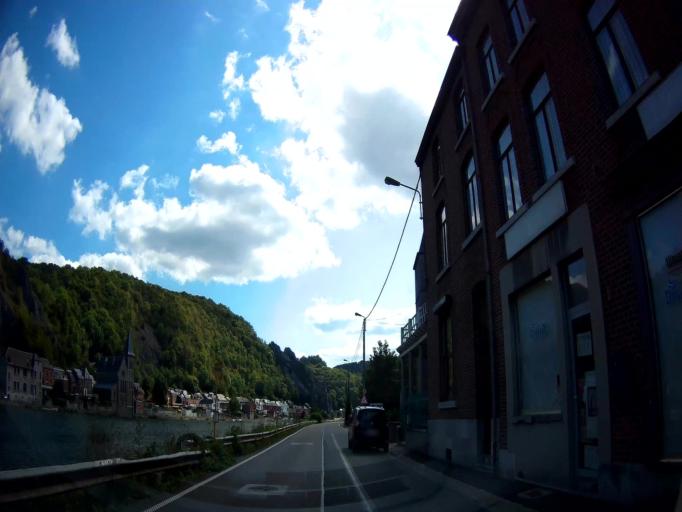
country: BE
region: Wallonia
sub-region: Province de Namur
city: Dinant
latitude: 50.2486
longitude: 4.9181
